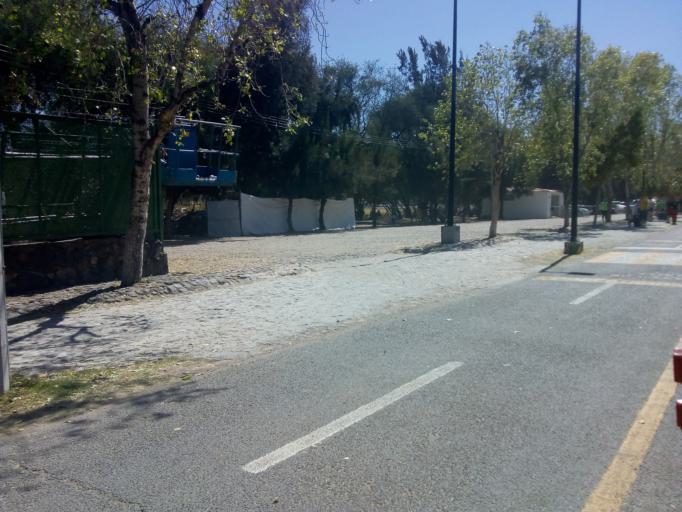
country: MX
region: Guanajuato
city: Leon
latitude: 21.1730
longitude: -101.6810
